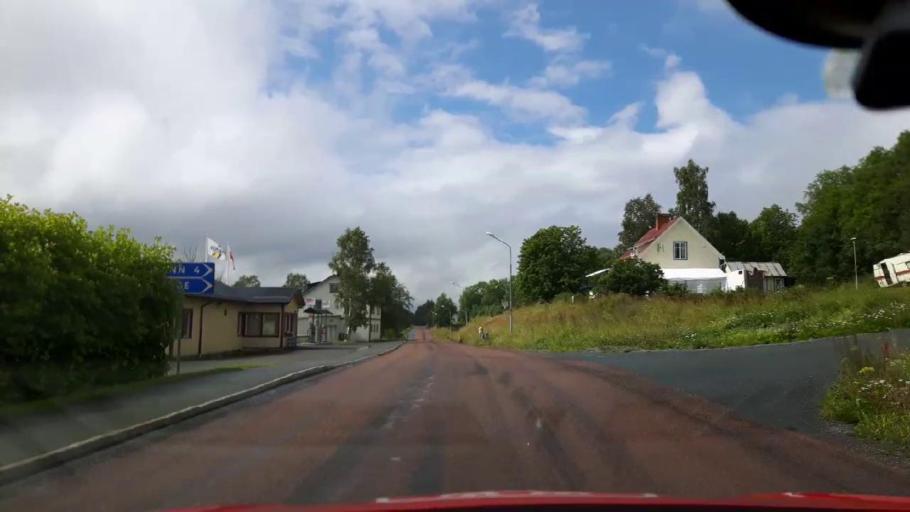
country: SE
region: Jaemtland
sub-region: Krokoms Kommun
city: Valla
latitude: 63.3857
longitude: 13.9319
